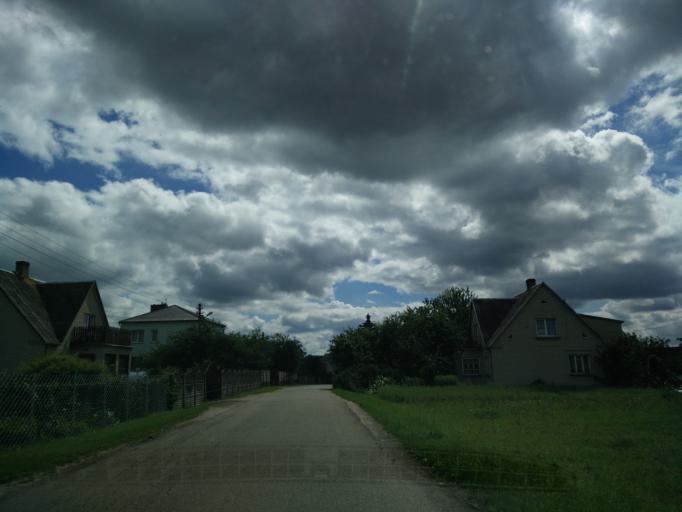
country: LT
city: Trakai
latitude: 54.6100
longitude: 24.9864
